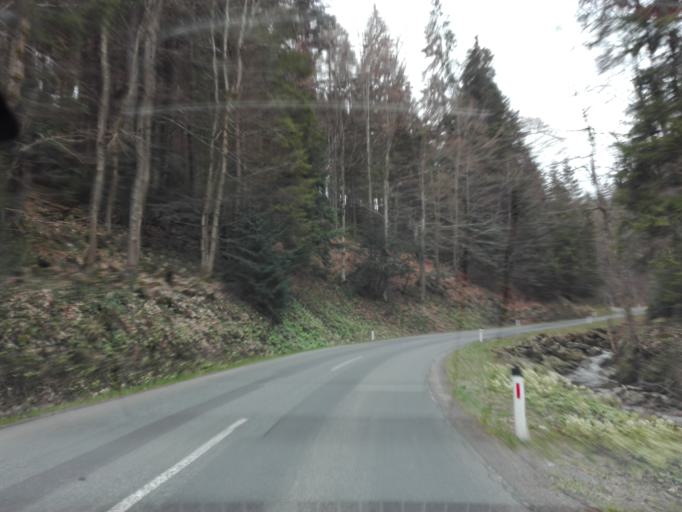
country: AT
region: Upper Austria
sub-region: Politischer Bezirk Rohrbach
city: Ulrichsberg
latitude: 48.7245
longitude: 13.8908
